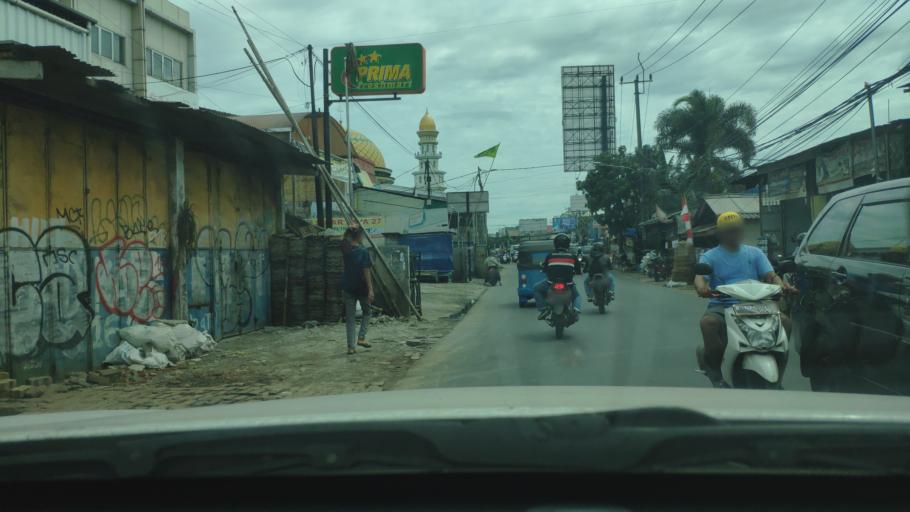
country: ID
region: West Java
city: Ciputat
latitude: -6.2235
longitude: 106.7054
